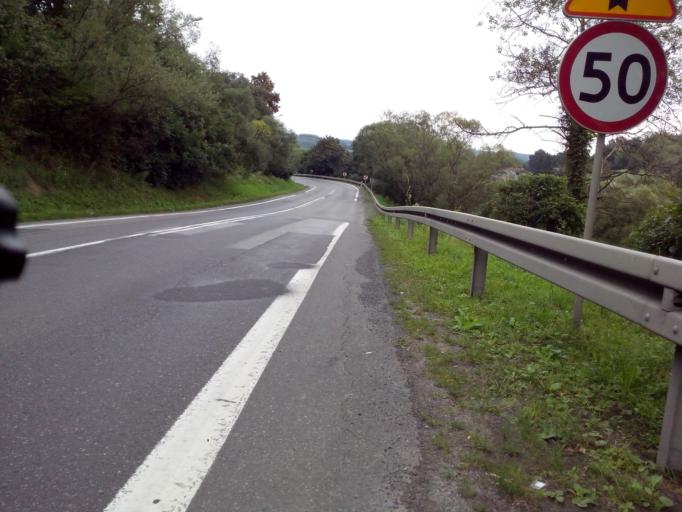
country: PL
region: Subcarpathian Voivodeship
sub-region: Powiat brzozowski
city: Domaradz
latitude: 49.7816
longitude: 21.9485
